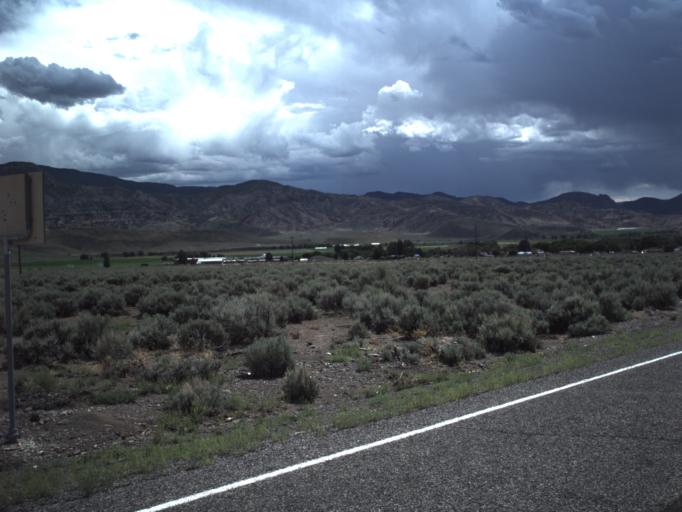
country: US
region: Utah
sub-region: Piute County
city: Junction
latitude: 38.2470
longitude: -112.2357
